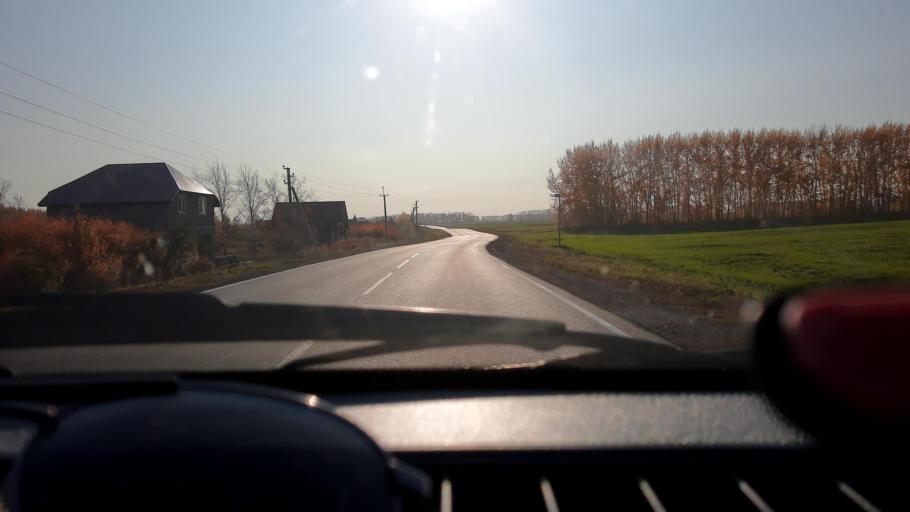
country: RU
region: Bashkortostan
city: Kabakovo
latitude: 54.4841
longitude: 55.9780
